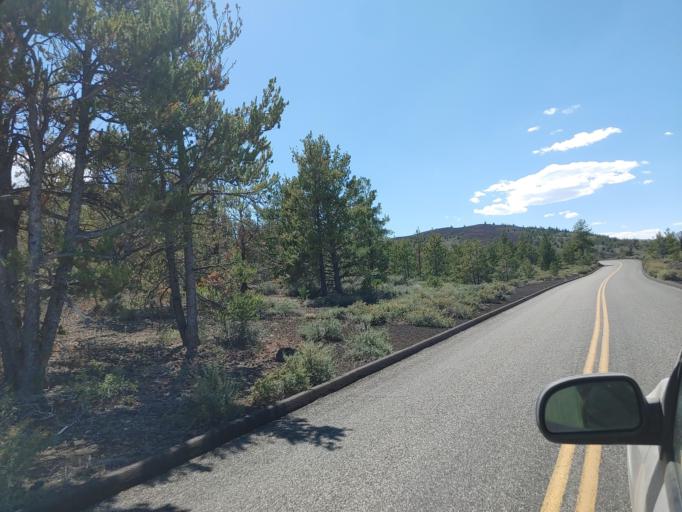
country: US
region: Idaho
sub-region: Butte County
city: Arco
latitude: 43.4540
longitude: -113.5494
